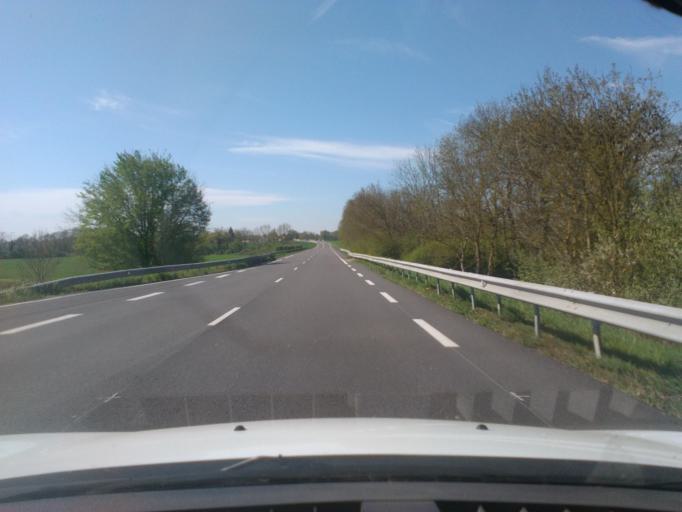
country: FR
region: Rhone-Alpes
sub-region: Departement de l'Ain
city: Villars-les-Dombes
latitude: 46.0544
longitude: 5.0748
